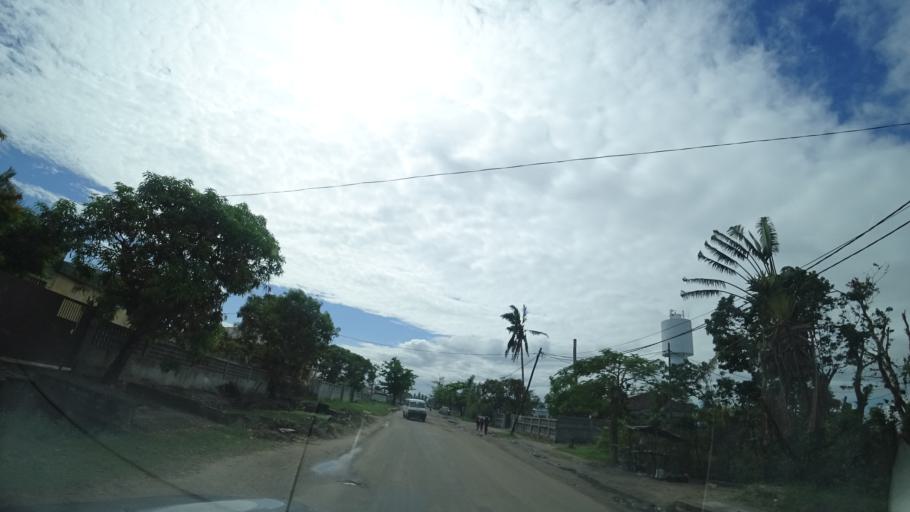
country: MZ
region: Sofala
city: Beira
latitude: -19.7596
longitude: 34.8648
